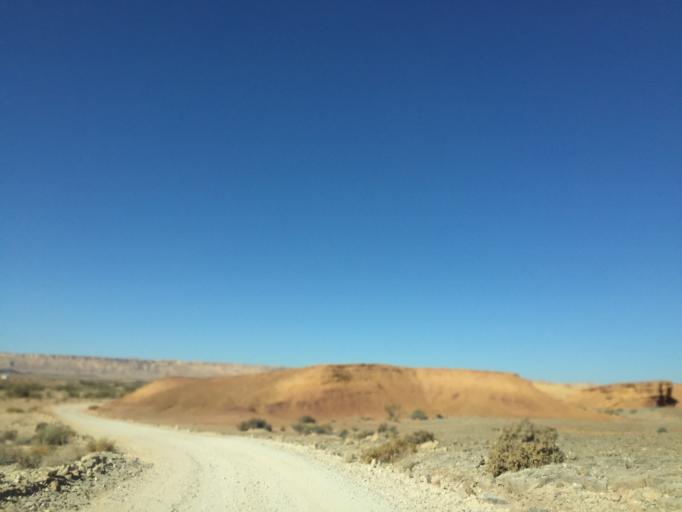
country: IL
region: Southern District
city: Mitzpe Ramon
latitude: 30.6195
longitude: 34.9304
